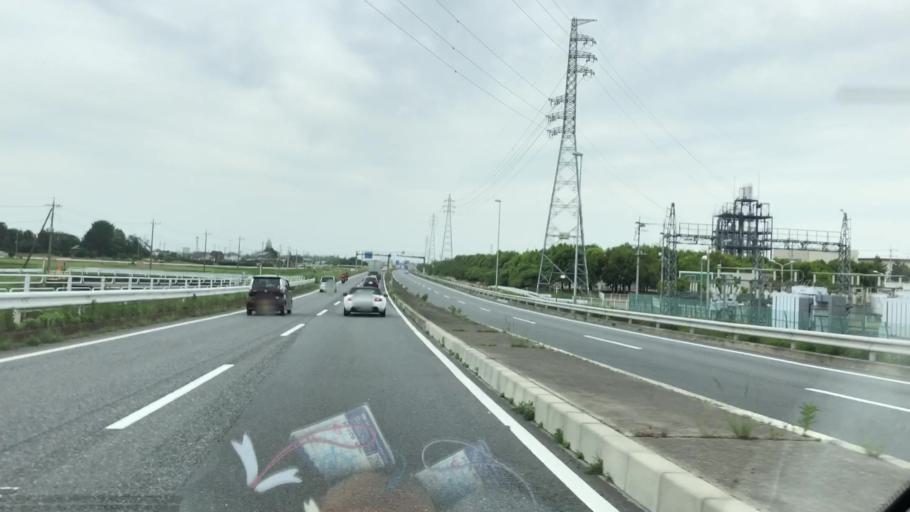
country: JP
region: Gunma
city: Sakai-nakajima
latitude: 36.2711
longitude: 139.2867
